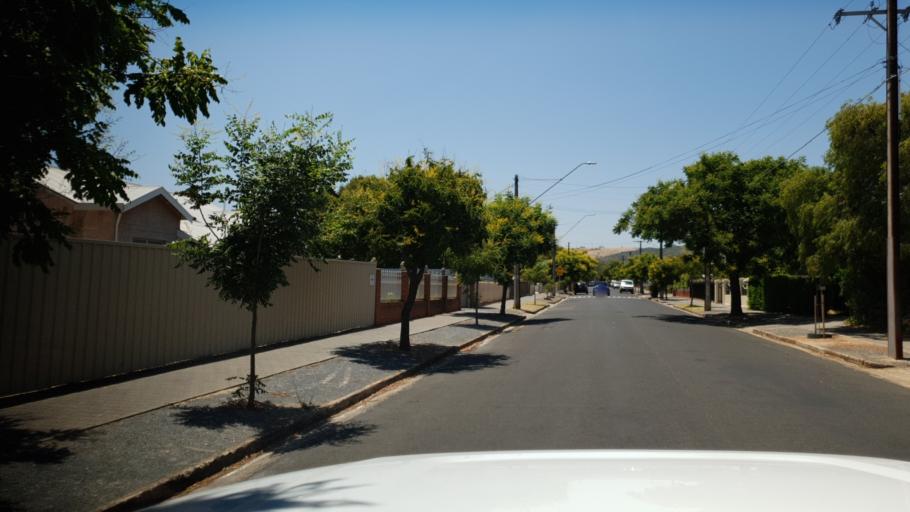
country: AU
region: South Australia
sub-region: Mitcham
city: Clapham
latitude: -34.9880
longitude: 138.5874
